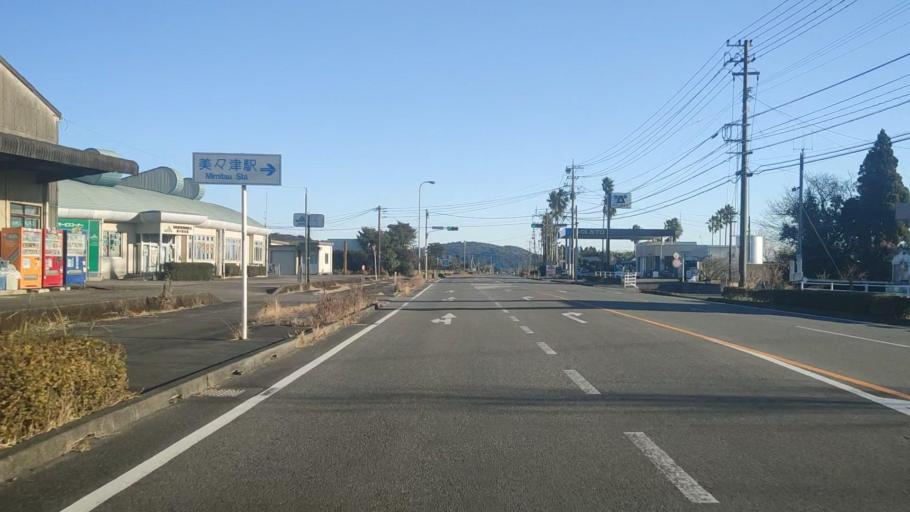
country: JP
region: Miyazaki
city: Takanabe
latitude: 32.3238
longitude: 131.5978
